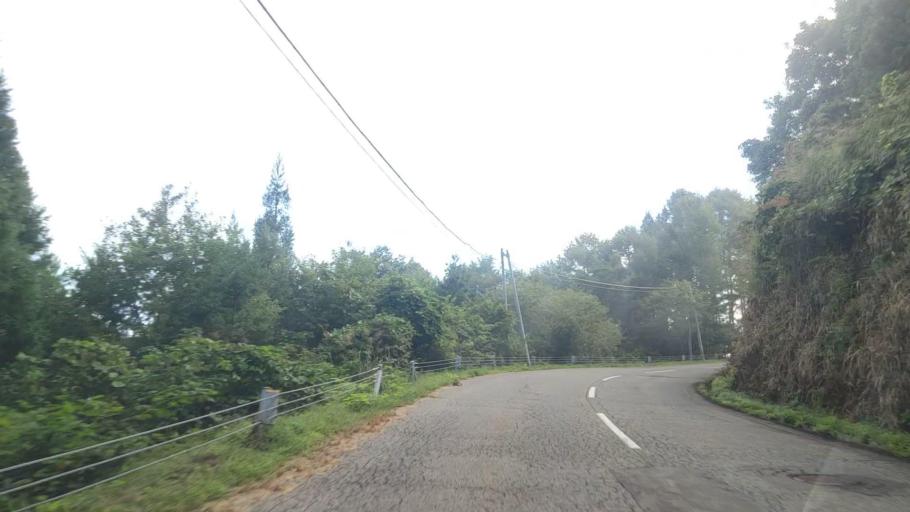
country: JP
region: Nagano
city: Iiyama
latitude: 36.8225
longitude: 138.4180
